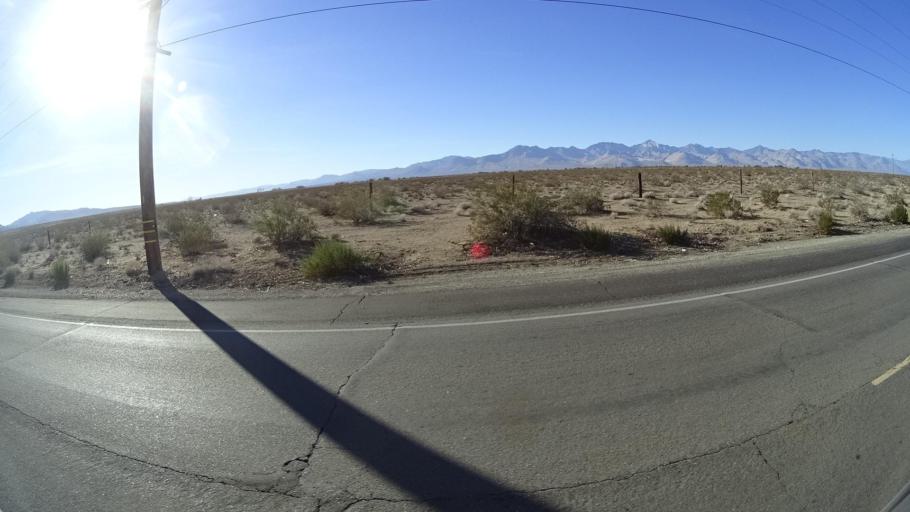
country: US
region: California
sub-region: Kern County
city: China Lake Acres
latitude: 35.6314
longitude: -117.7230
